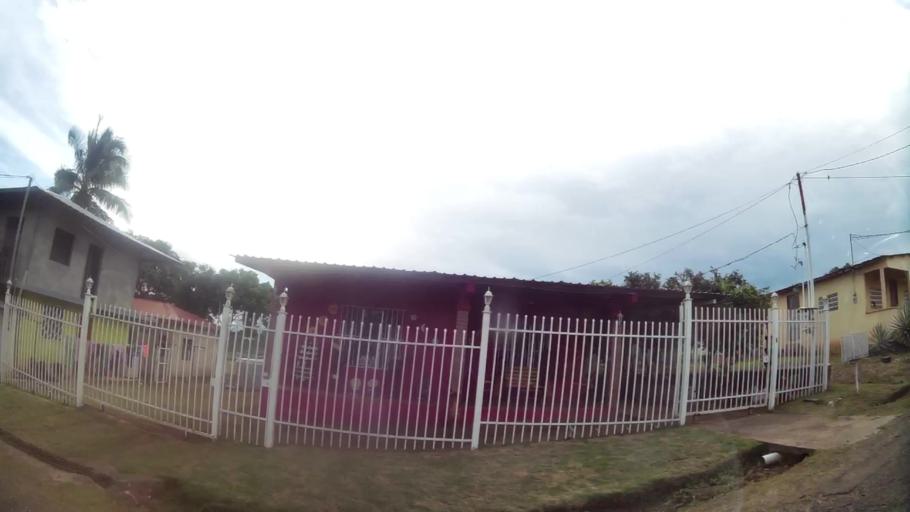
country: PA
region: Panama
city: El Coco
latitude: 8.8771
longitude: -79.8096
